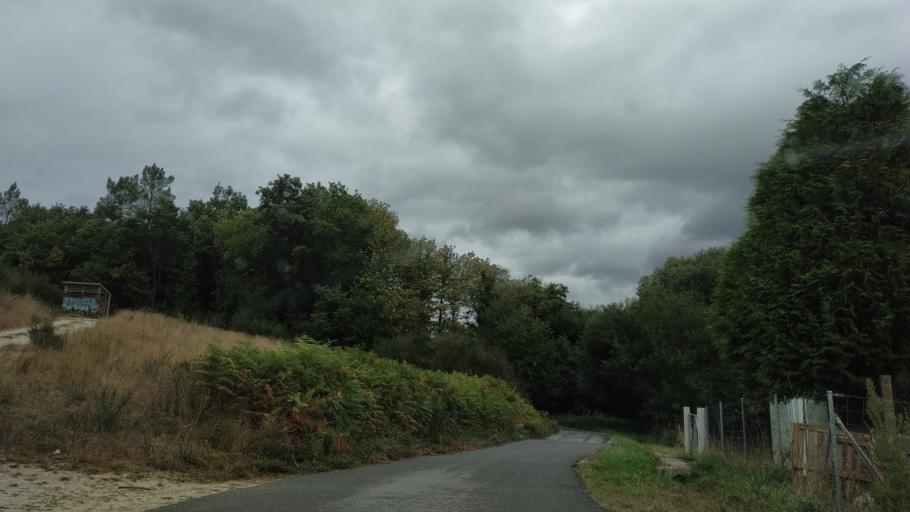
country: ES
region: Galicia
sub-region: Provincia de Lugo
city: Lugo
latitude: 42.9961
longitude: -7.5755
